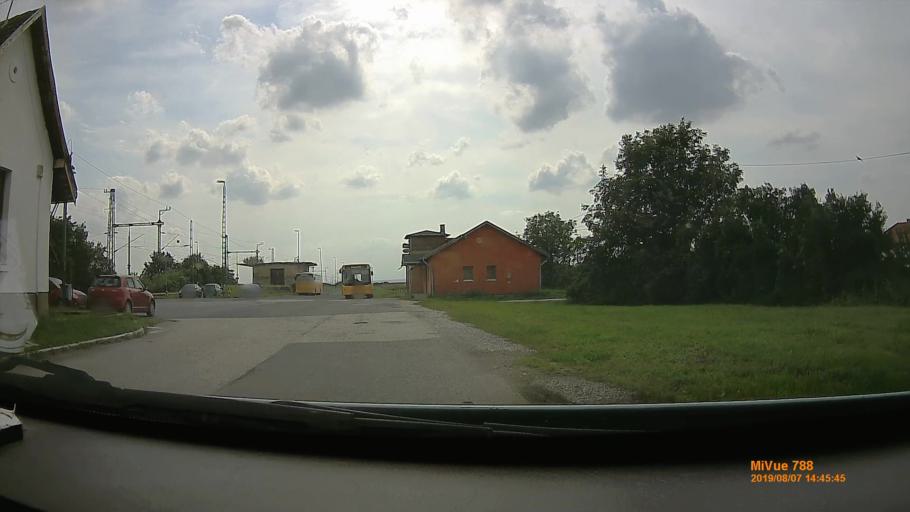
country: HU
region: Borsod-Abauj-Zemplen
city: Halmaj
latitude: 48.2467
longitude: 20.9912
